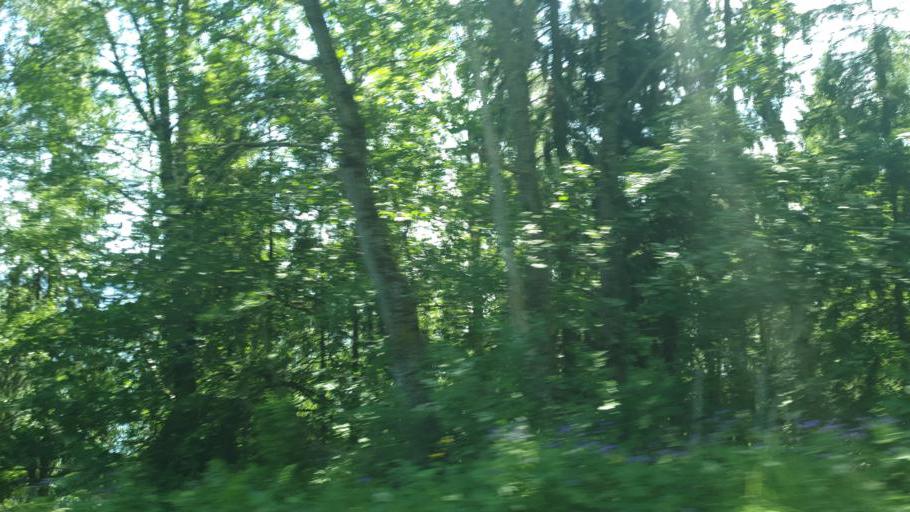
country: NO
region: Nord-Trondelag
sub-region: Leksvik
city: Leksvik
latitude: 63.6953
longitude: 10.7092
